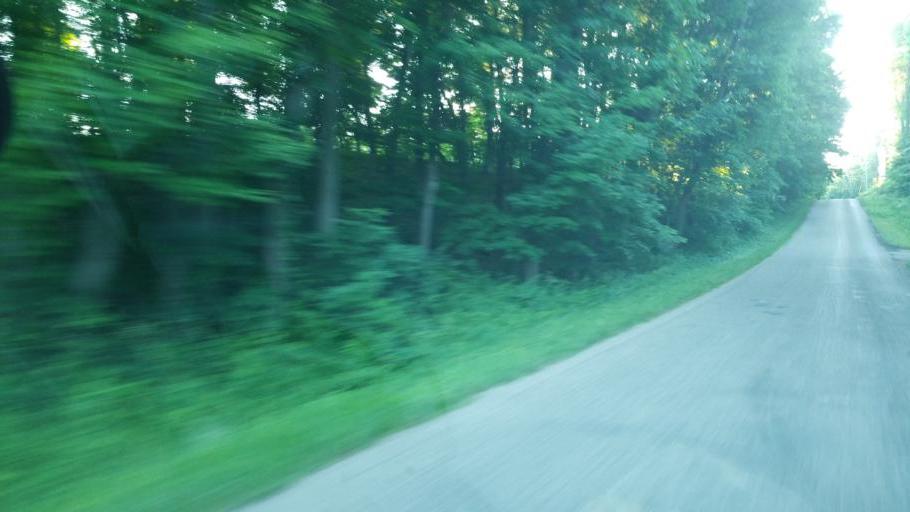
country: US
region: Ohio
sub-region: Richland County
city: Lexington
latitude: 40.6446
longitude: -82.5725
